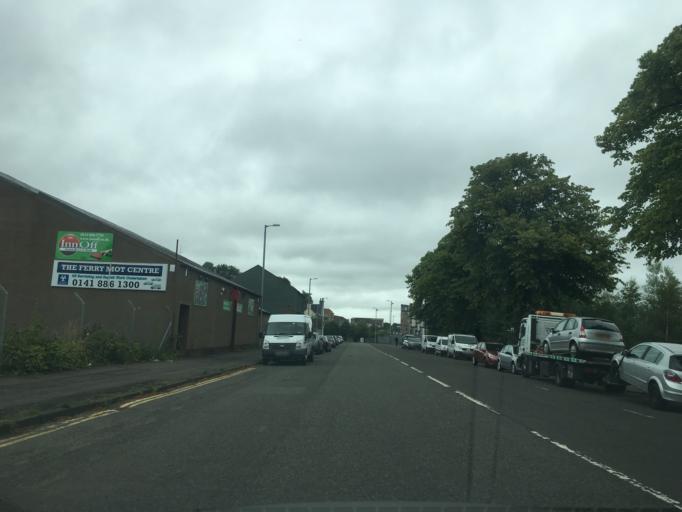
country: GB
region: Scotland
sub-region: Renfrewshire
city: Renfrew
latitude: 55.8844
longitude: -4.3844
